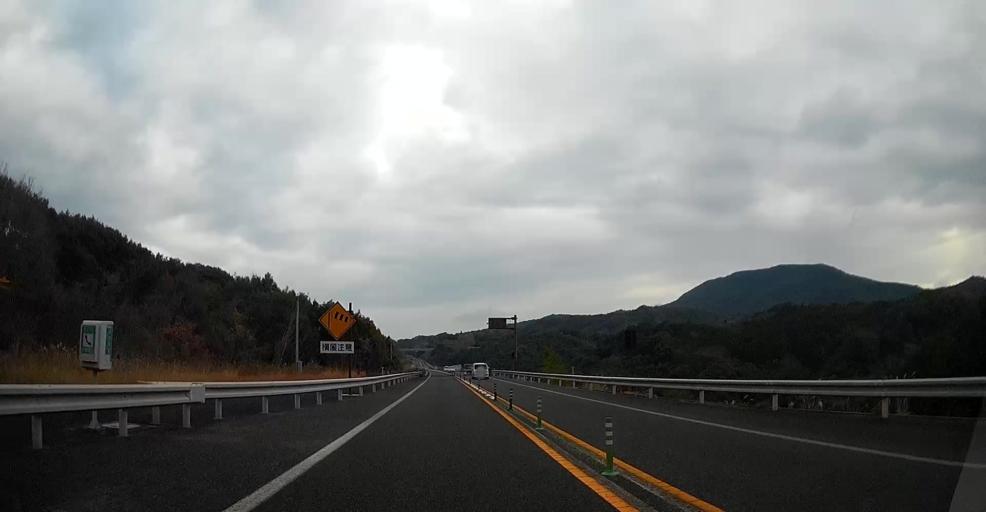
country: JP
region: Kumamoto
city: Hondo
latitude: 32.5080
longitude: 130.3385
